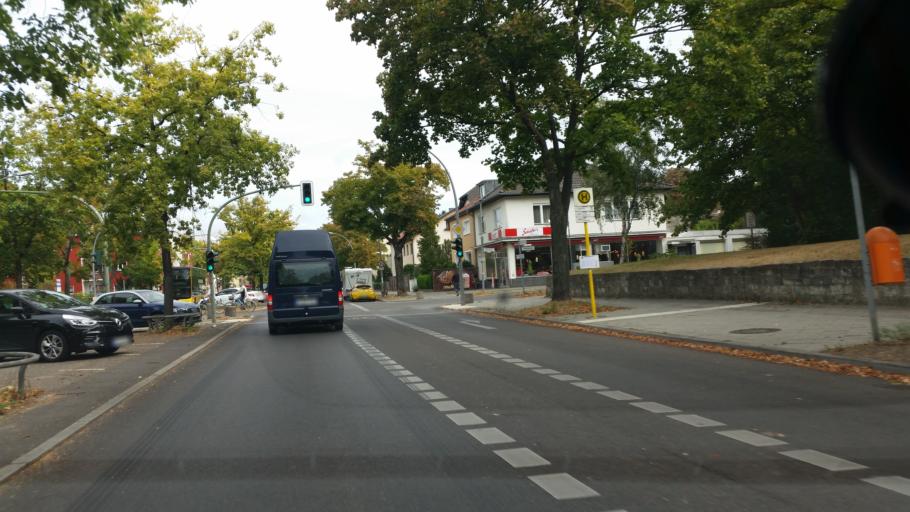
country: DE
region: Berlin
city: Mariendorf
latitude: 52.4433
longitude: 13.3985
